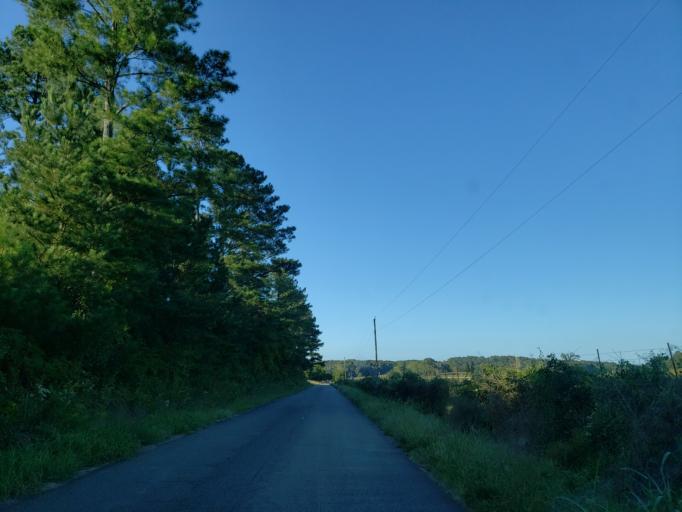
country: US
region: Georgia
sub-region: Bartow County
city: Rydal
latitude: 34.3211
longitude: -84.7297
